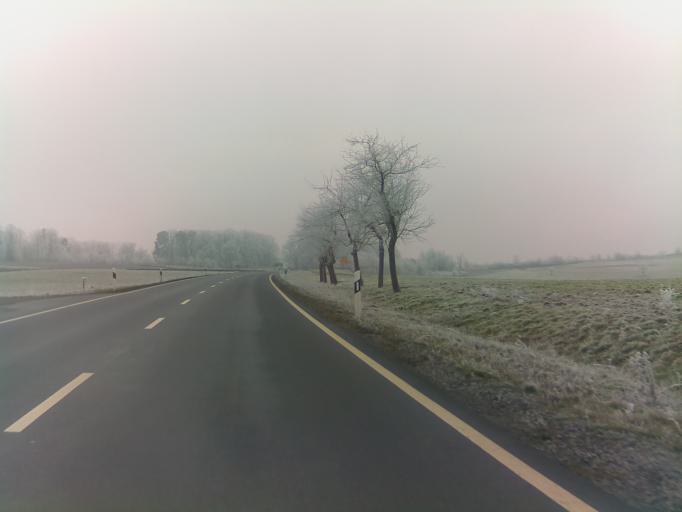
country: DE
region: Baden-Wuerttemberg
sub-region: Regierungsbezirk Stuttgart
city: Boxberg
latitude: 49.4664
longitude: 9.6165
